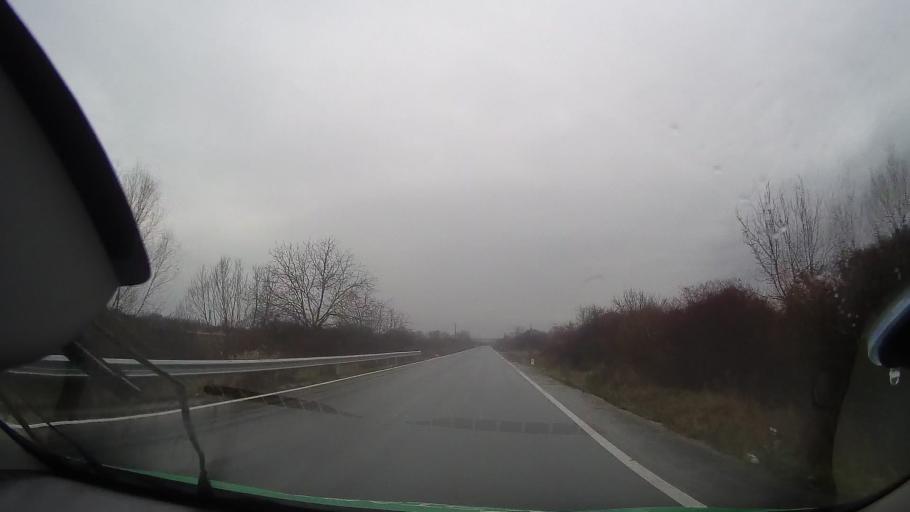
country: RO
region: Bihor
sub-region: Comuna Tinca
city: Tinca
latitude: 46.7391
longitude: 21.9409
